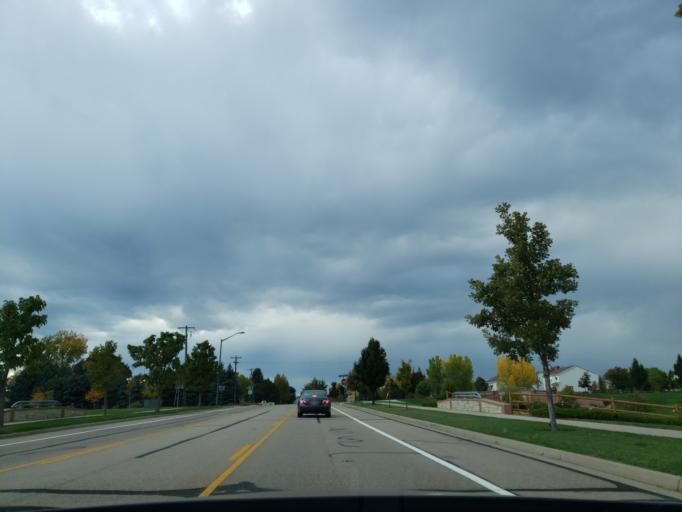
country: US
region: Colorado
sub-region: Larimer County
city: Fort Collins
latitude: 40.6248
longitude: -105.0375
